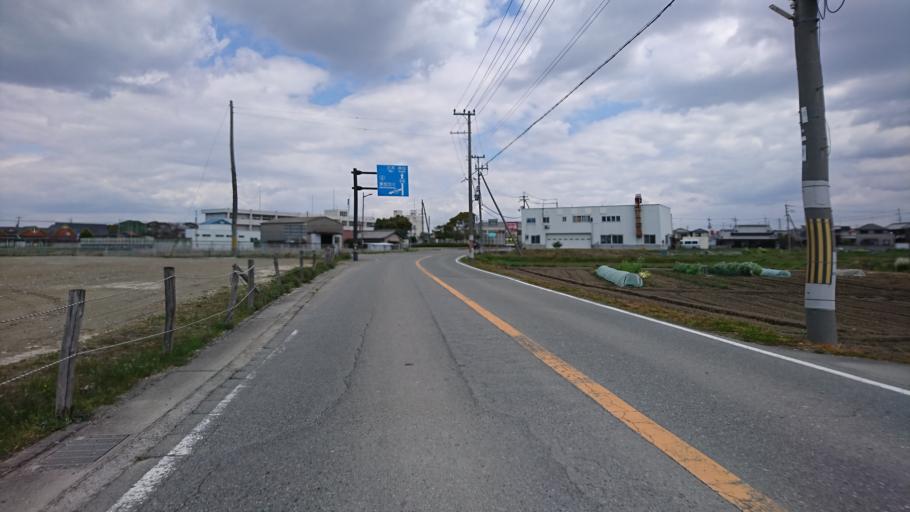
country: JP
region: Hyogo
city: Miki
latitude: 34.7524
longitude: 134.9414
